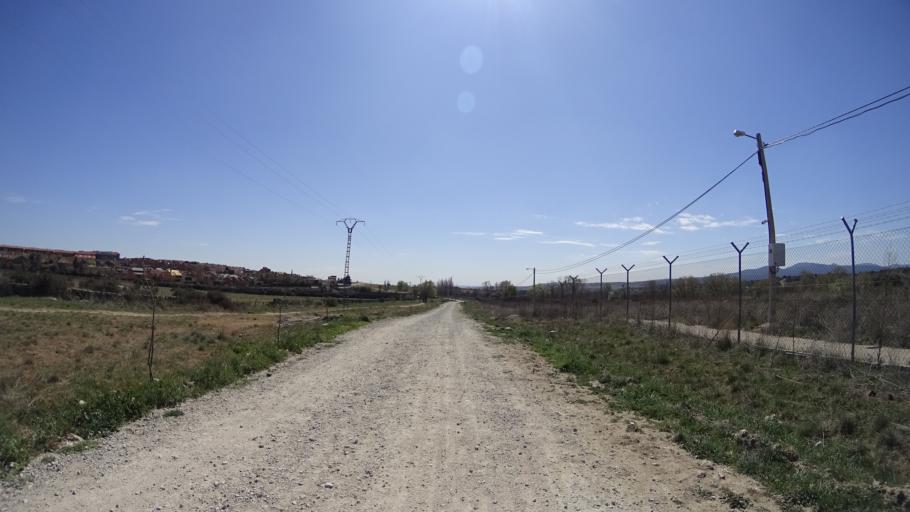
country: ES
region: Madrid
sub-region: Provincia de Madrid
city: Colmenar Viejo
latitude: 40.6751
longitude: -3.7847
